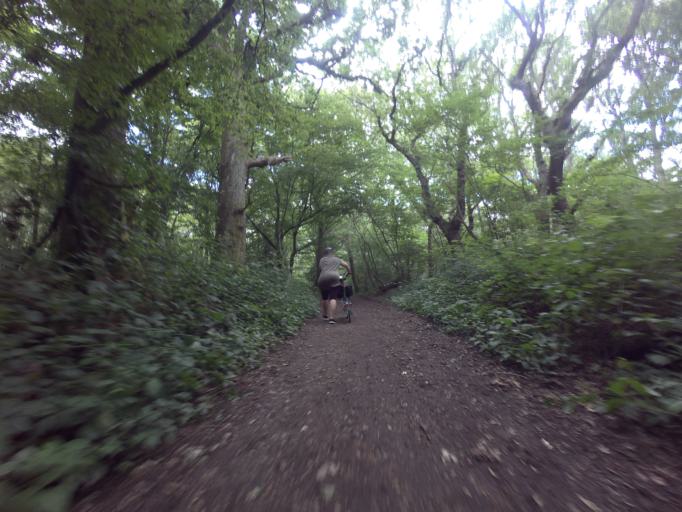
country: GB
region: England
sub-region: East Sussex
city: Hailsham
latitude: 50.8356
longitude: 0.2279
